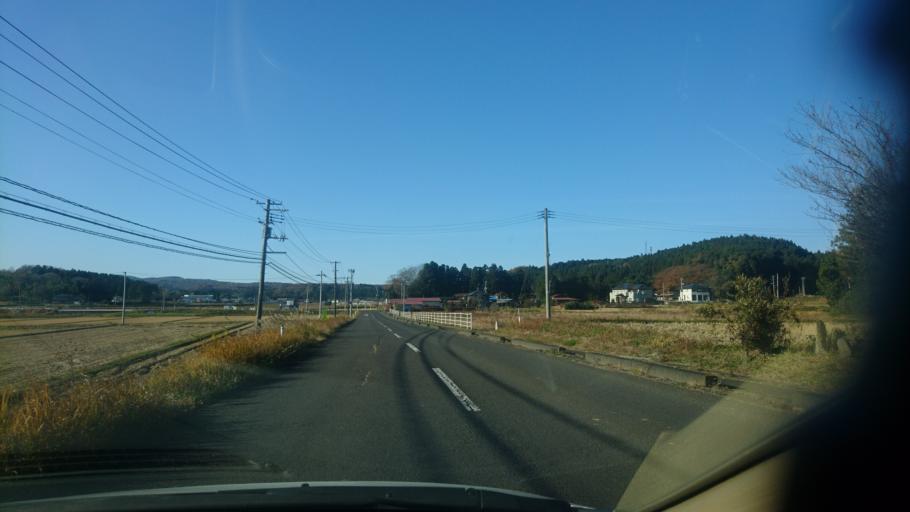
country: JP
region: Miyagi
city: Tomiya
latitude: 38.4718
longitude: 140.8564
